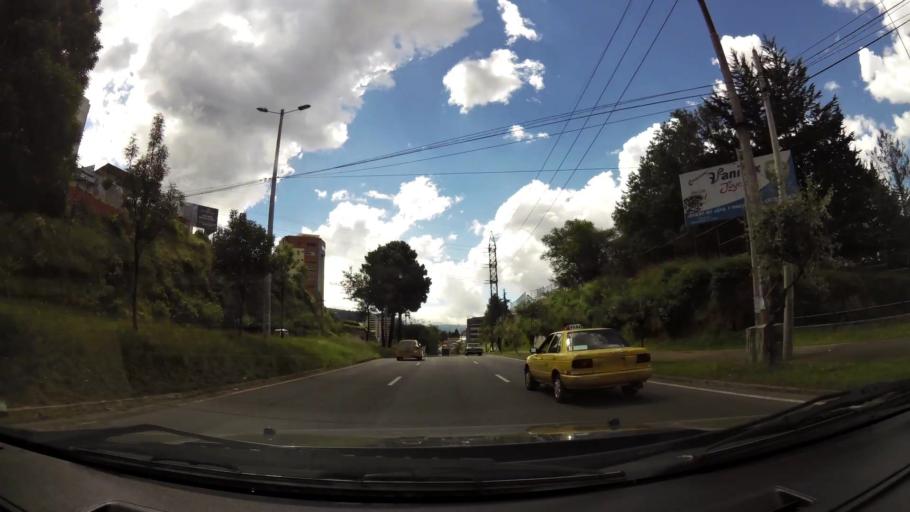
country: EC
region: Pichincha
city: Quito
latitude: -0.1587
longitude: -78.4962
